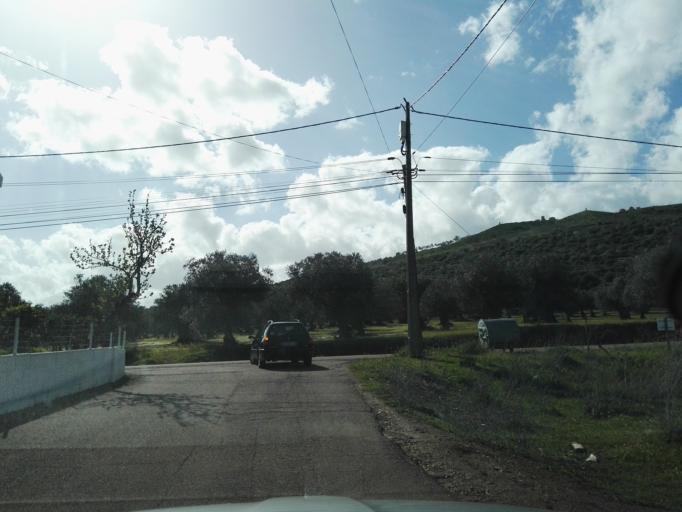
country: PT
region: Portalegre
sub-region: Elvas
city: Elvas
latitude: 38.8919
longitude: -7.1561
